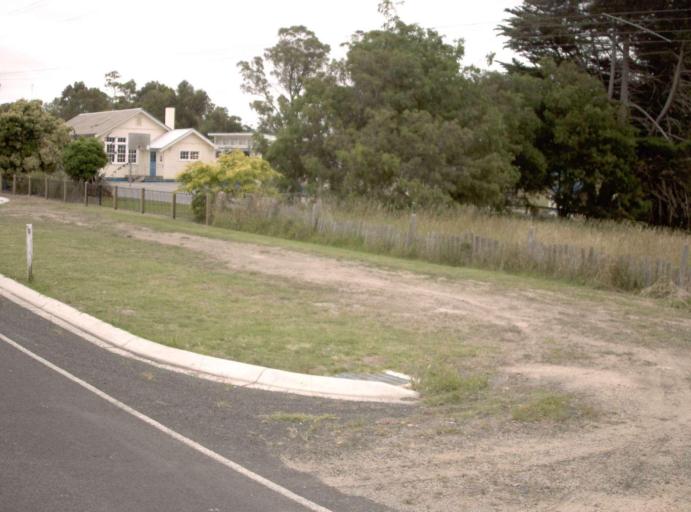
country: AU
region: Victoria
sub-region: Wellington
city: Sale
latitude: -38.5260
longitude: 146.8771
